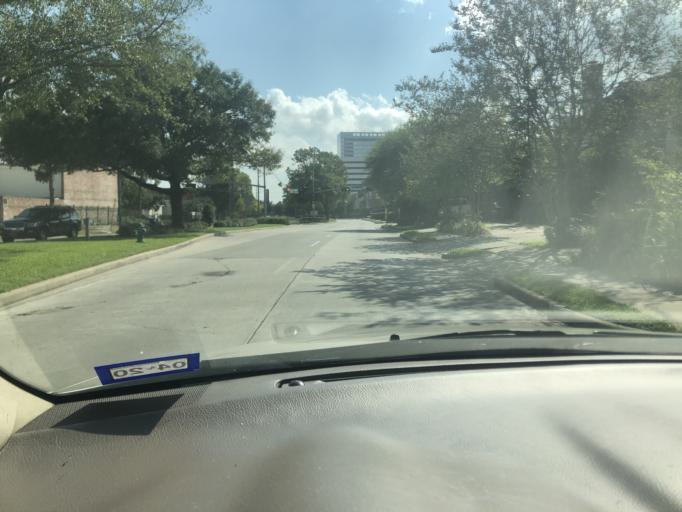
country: US
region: Texas
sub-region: Harris County
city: Bunker Hill Village
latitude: 29.7473
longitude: -95.5659
